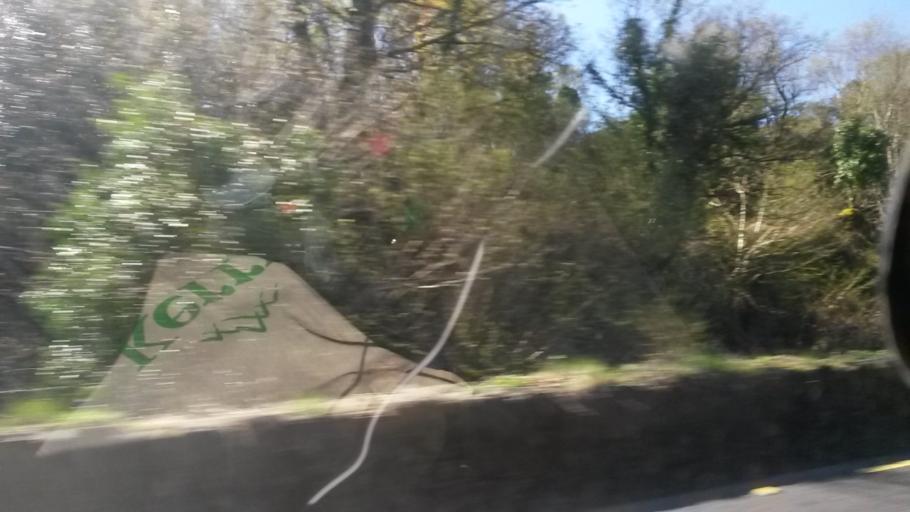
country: IE
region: Munster
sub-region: Ciarrai
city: Cill Airne
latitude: 51.9773
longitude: -9.3315
